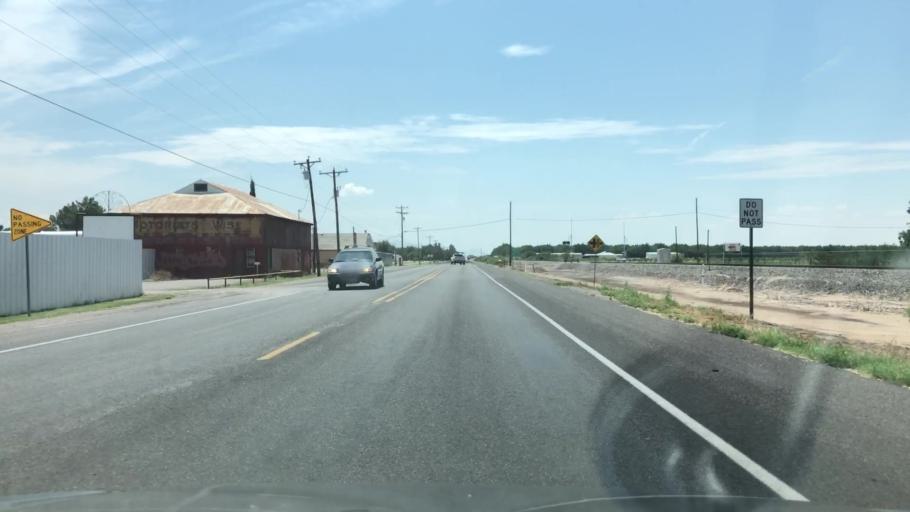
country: US
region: New Mexico
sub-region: Dona Ana County
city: Mesquite
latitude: 32.2101
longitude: -106.7254
